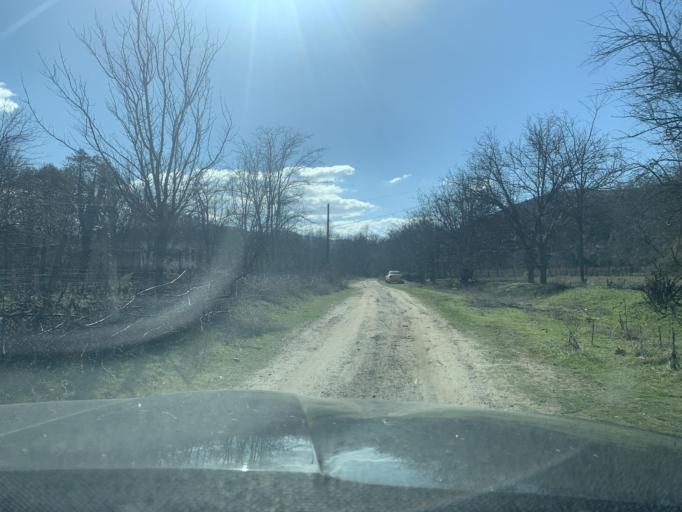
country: MK
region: Demir Kapija
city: Demir Kapija
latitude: 41.3964
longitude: 22.2179
